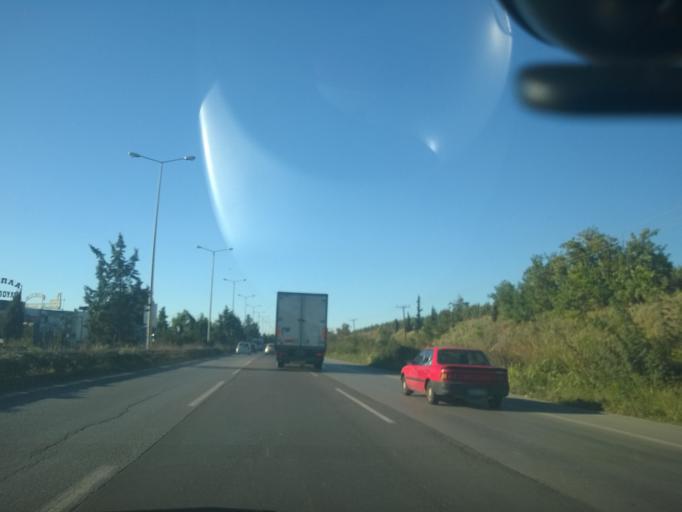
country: GR
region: Central Macedonia
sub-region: Nomos Thessalonikis
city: Pylaia
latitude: 40.5654
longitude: 22.9888
